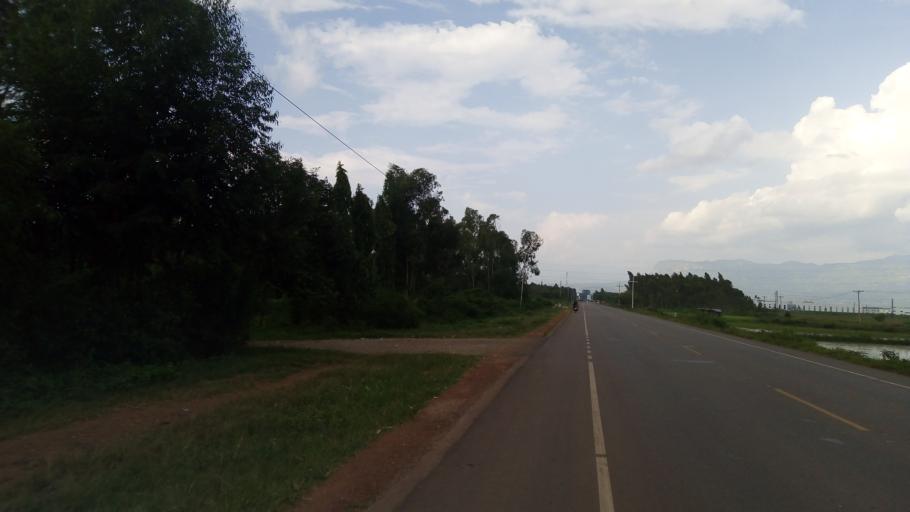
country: UG
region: Eastern Region
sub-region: Mbale District
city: Mbale
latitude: 1.0746
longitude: 34.1258
